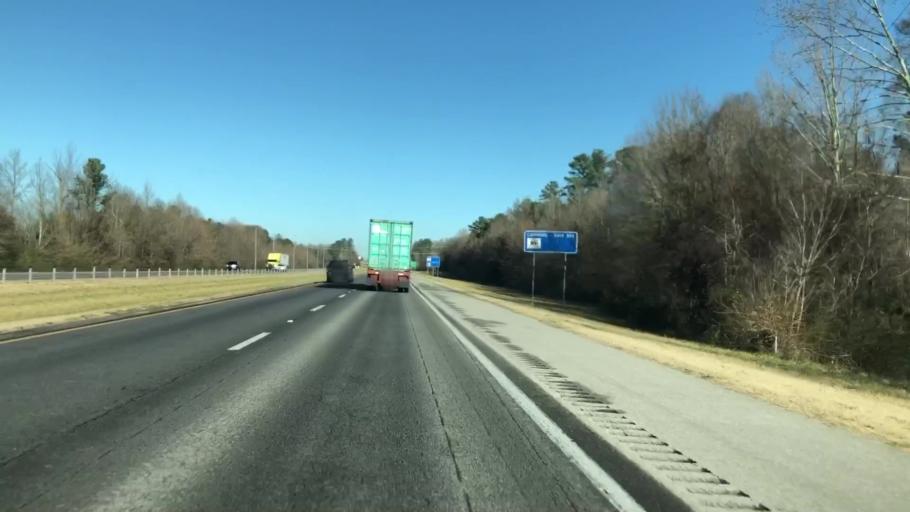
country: US
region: Alabama
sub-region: Limestone County
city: Athens
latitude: 34.8183
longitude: -86.9387
